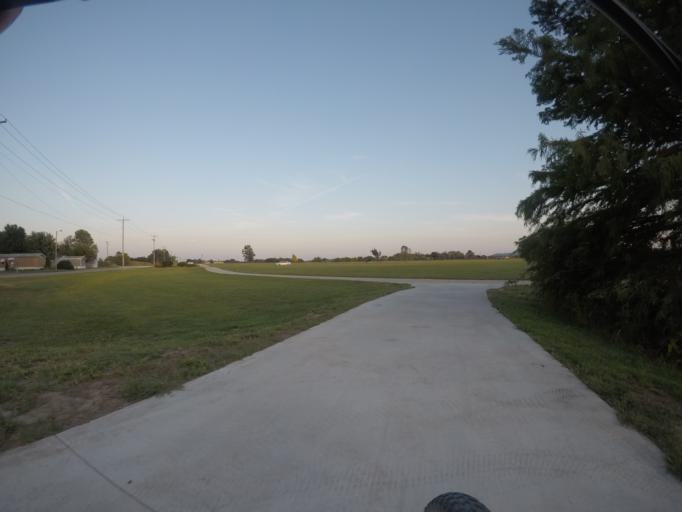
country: US
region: Kansas
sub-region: Riley County
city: Manhattan
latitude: 39.2039
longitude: -96.5496
